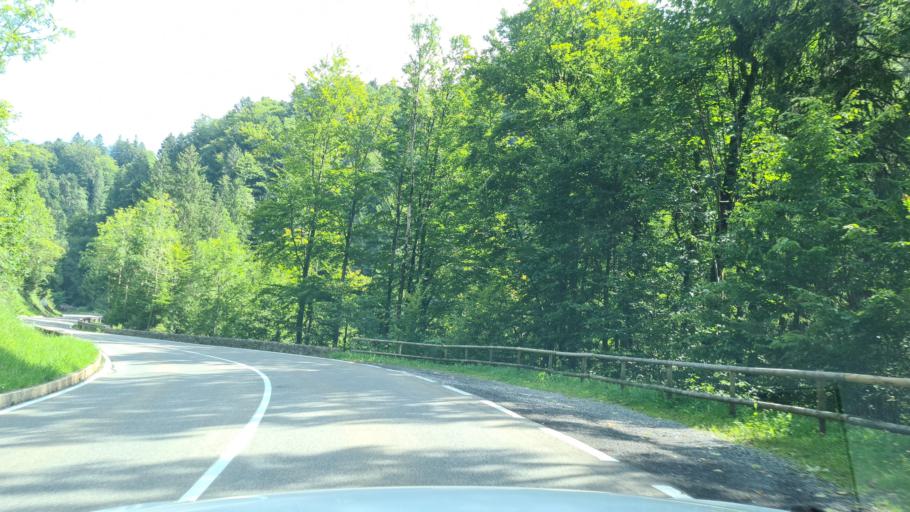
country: AT
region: Vorarlberg
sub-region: Politischer Bezirk Bregenz
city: Bildstein
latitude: 47.4438
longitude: 9.7846
